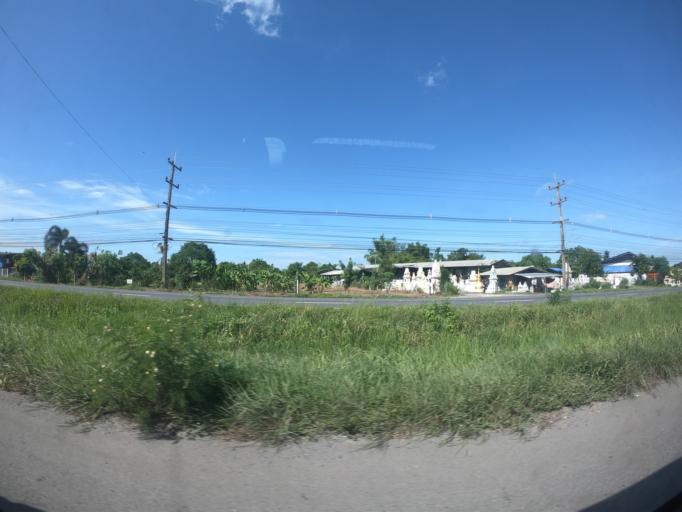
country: TH
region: Nakhon Nayok
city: Ban Na
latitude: 14.2474
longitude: 101.1062
